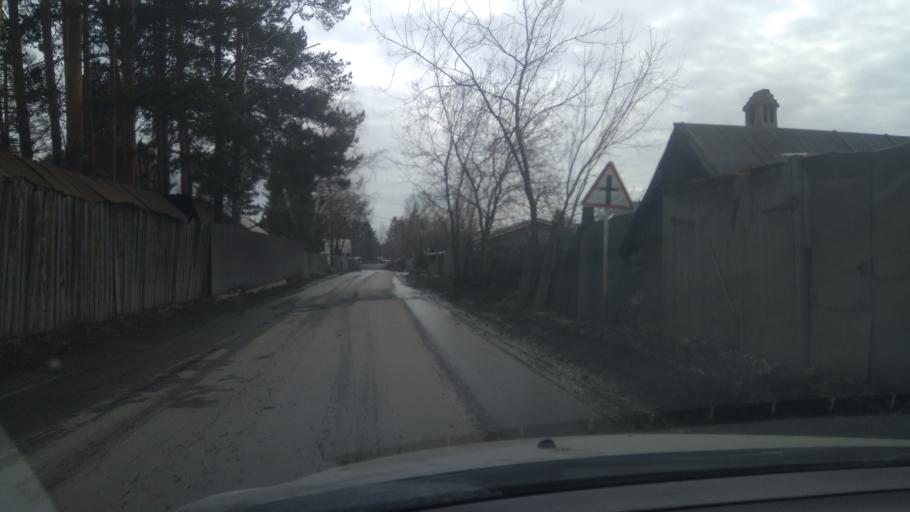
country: RU
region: Sverdlovsk
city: Severka
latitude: 56.8498
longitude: 60.3847
